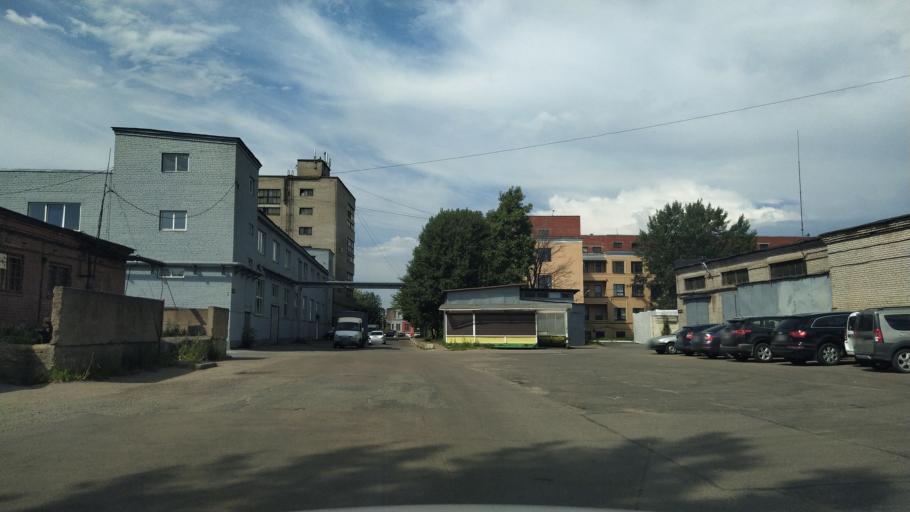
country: RU
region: Leningrad
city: Finlyandskiy
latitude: 59.9625
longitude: 30.3650
